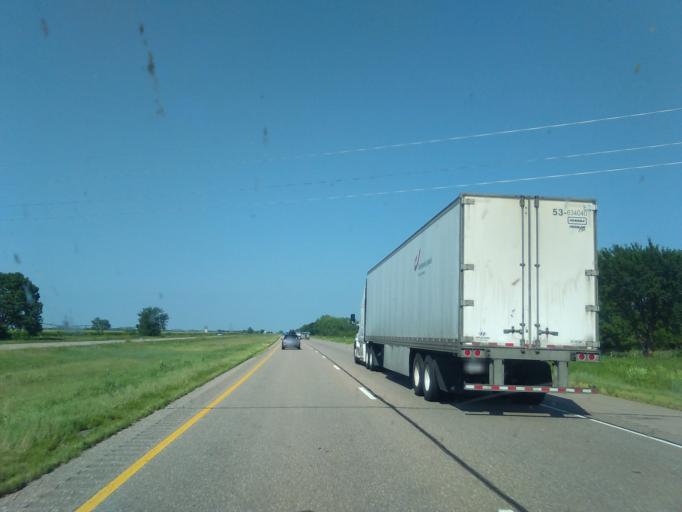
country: US
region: Nebraska
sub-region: Buffalo County
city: Shelton
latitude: 40.7285
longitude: -98.6649
